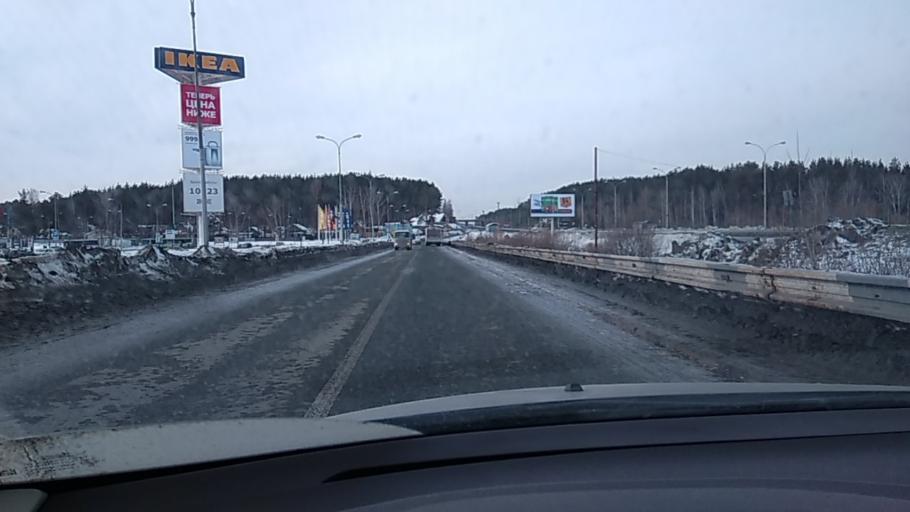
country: RU
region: Sverdlovsk
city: Shirokaya Rechka
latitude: 56.8259
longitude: 60.5039
